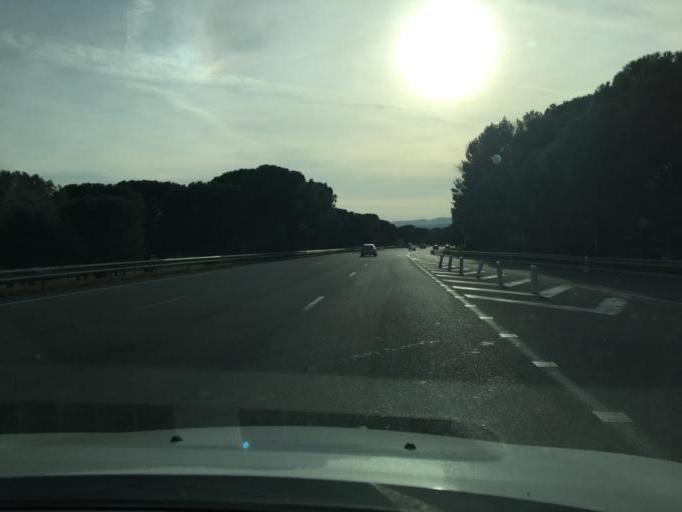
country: FR
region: Provence-Alpes-Cote d'Azur
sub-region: Departement du Var
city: Vidauban
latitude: 43.4151
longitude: 6.4517
